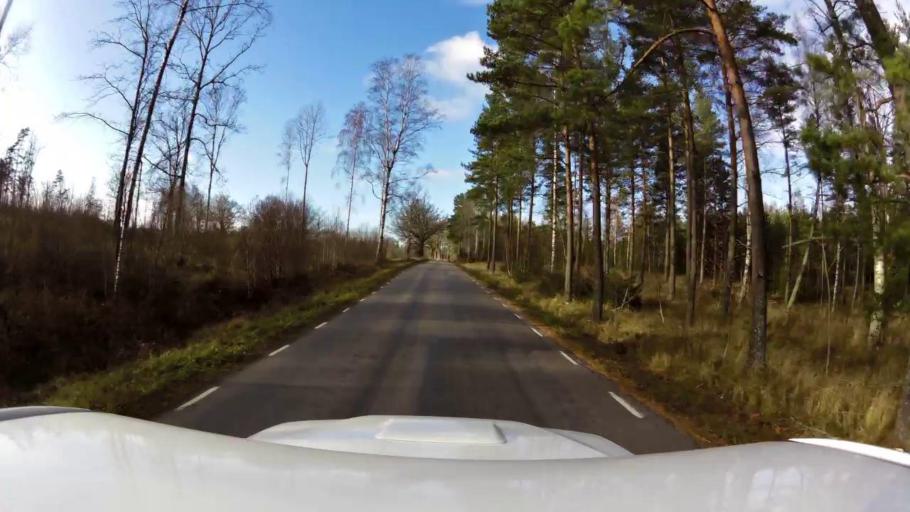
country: SE
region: OEstergoetland
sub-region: Linkopings Kommun
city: Sturefors
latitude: 58.3202
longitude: 15.6572
